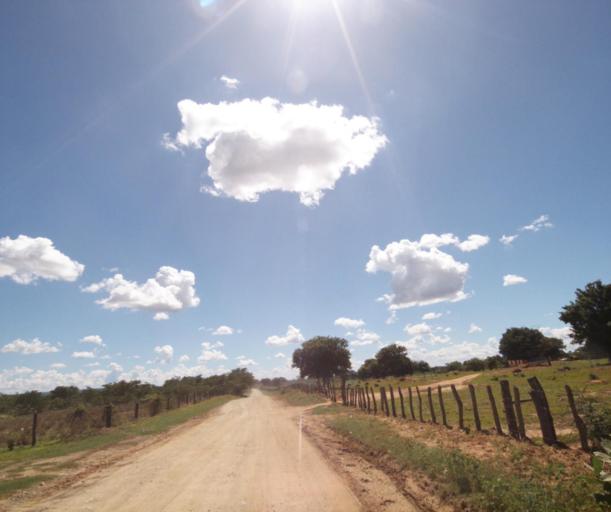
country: BR
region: Bahia
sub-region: Carinhanha
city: Carinhanha
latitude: -14.2211
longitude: -44.2941
